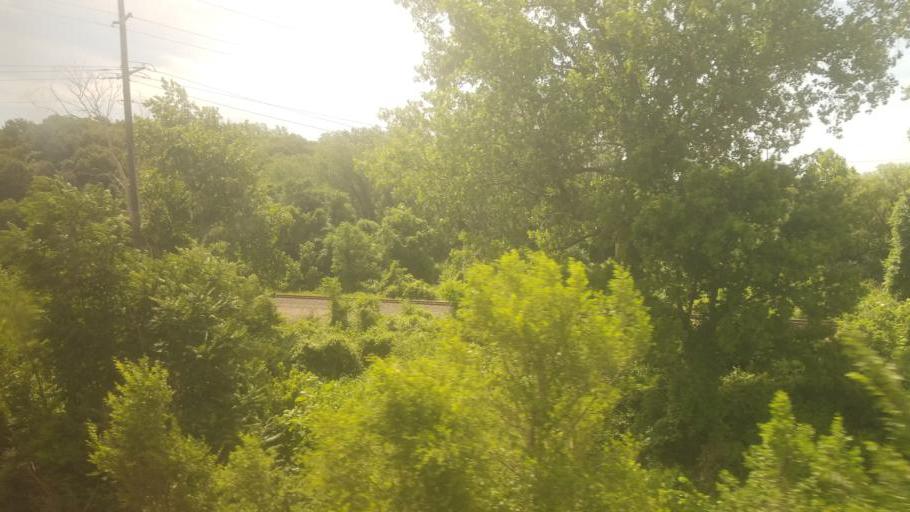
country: US
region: Missouri
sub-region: Jackson County
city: Sugar Creek
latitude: 39.1141
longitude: -94.4739
